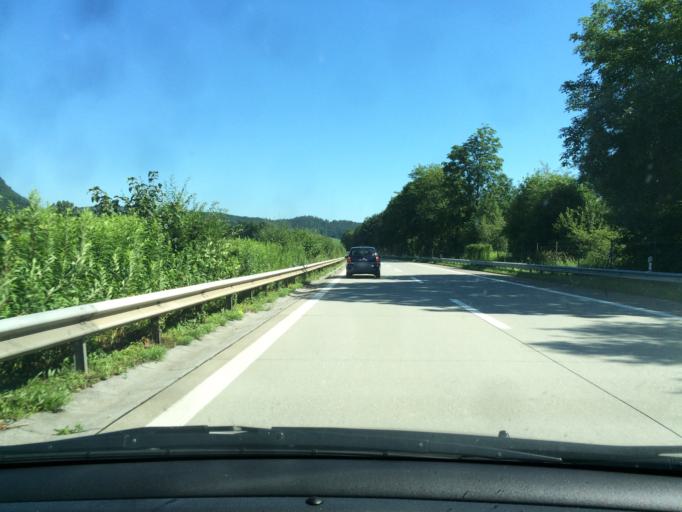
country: CH
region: Saint Gallen
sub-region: Wahlkreis Rheintal
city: Ruthi
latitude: 47.2886
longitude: 9.5505
